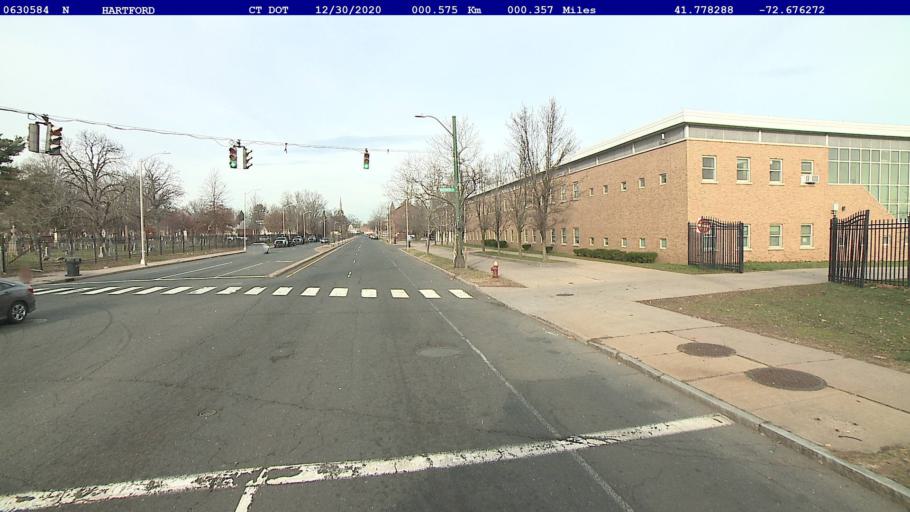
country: US
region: Connecticut
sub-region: Hartford County
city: Hartford
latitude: 41.7783
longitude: -72.6763
